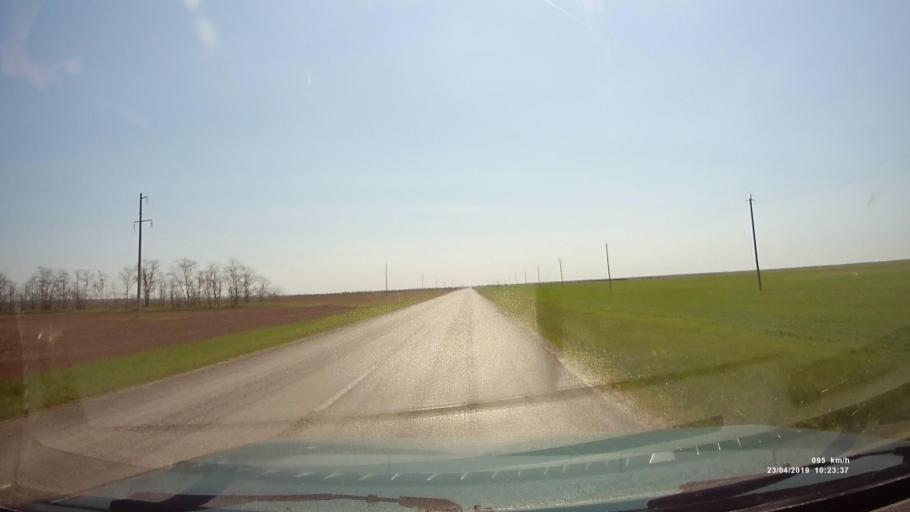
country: RU
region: Rostov
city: Sovetskoye
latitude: 46.6461
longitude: 42.4274
